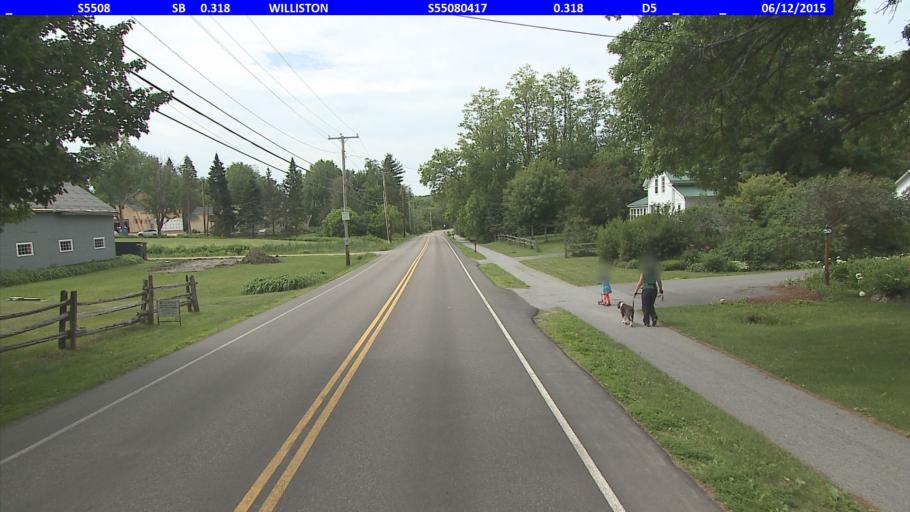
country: US
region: Vermont
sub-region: Chittenden County
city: Williston
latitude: 44.4414
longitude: -73.0652
